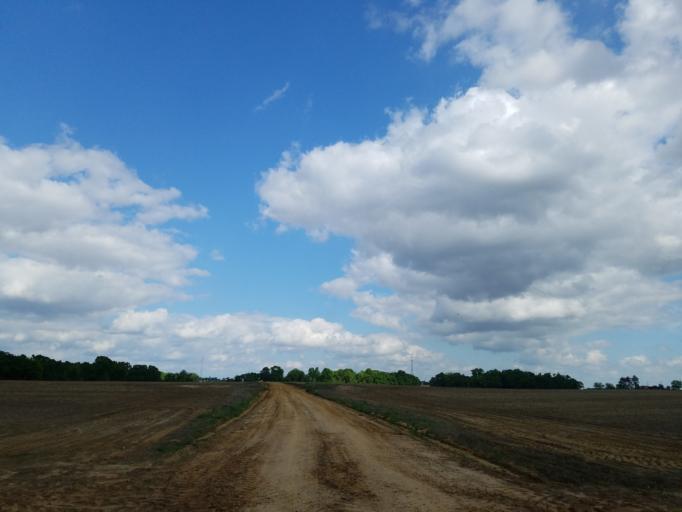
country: US
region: Georgia
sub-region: Dooly County
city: Vienna
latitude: 32.1764
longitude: -83.7804
